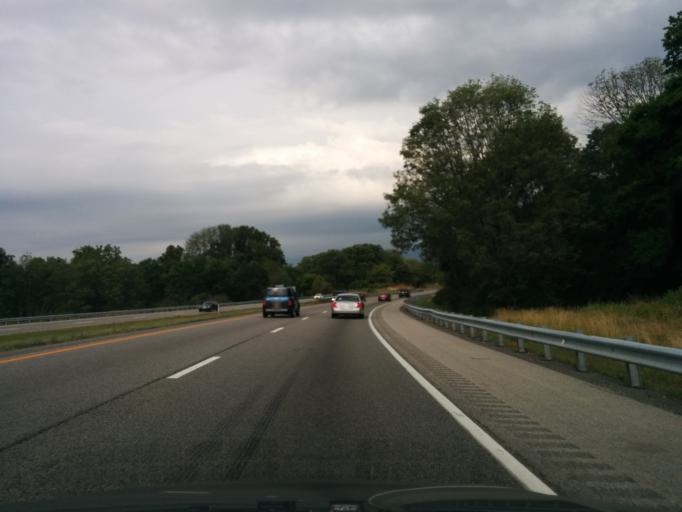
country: US
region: Delaware
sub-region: New Castle County
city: Claymont
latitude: 39.8039
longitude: -75.4679
